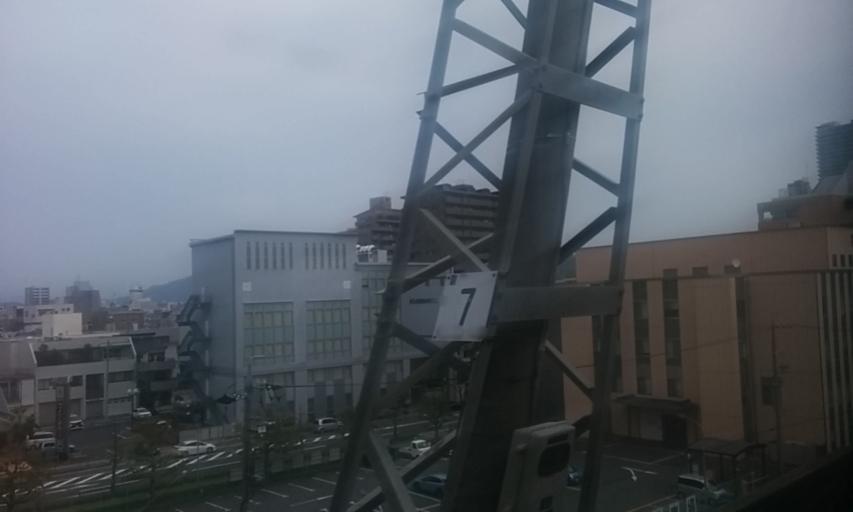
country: JP
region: Gifu
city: Gifu-shi
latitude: 35.4104
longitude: 136.7480
